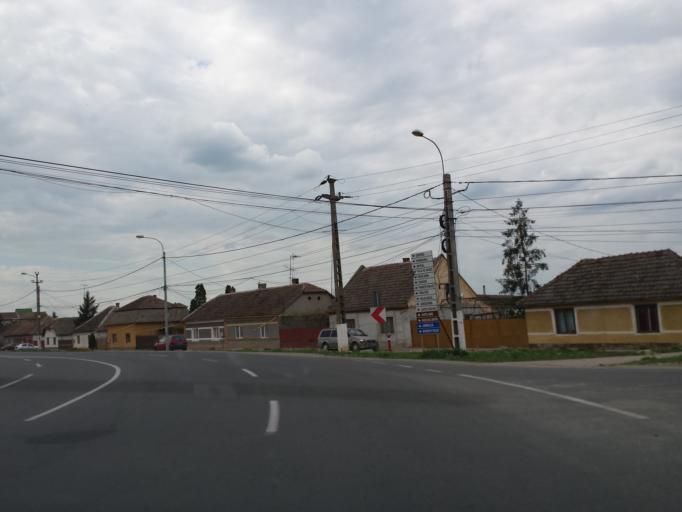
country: RO
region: Timis
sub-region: Oras Sannicolau Mare
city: Sannicolau Mare
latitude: 46.0665
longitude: 20.6419
